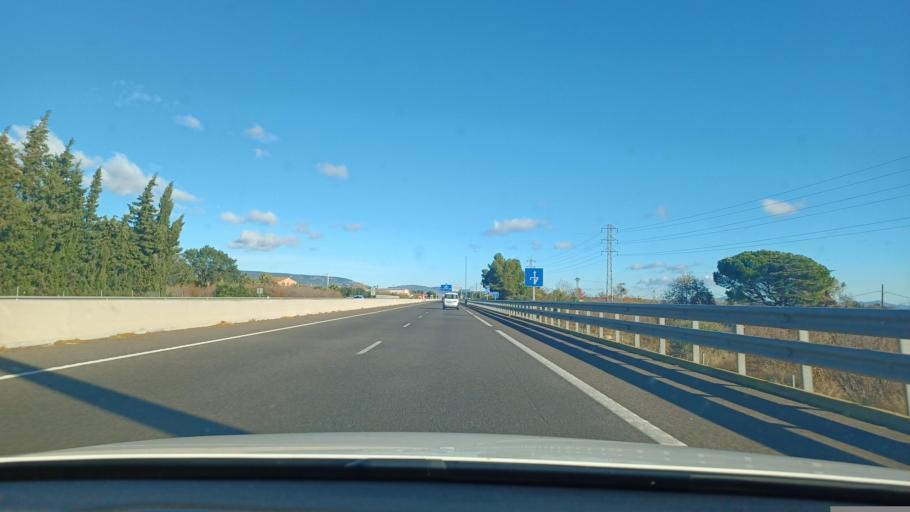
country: ES
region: Catalonia
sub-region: Provincia de Tarragona
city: La Selva
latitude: 41.1965
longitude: 1.1420
